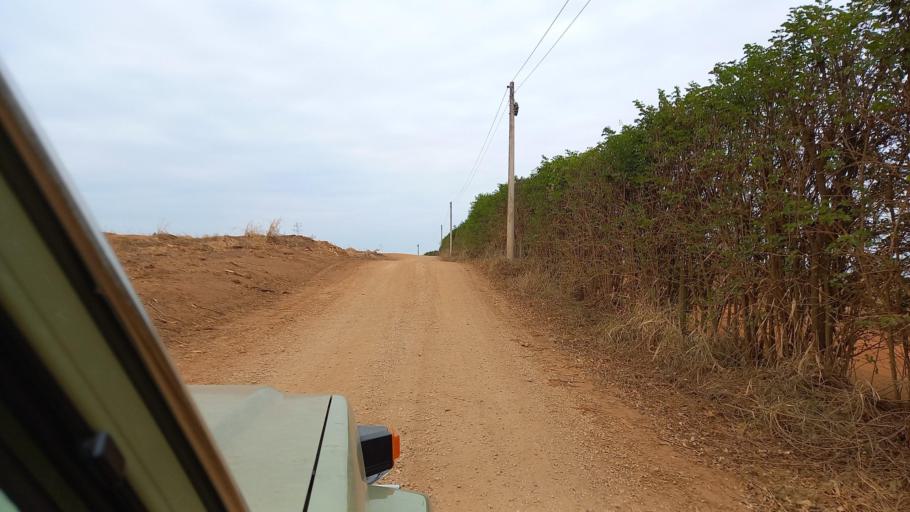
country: BR
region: Sao Paulo
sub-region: Moji-Guacu
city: Mogi-Gaucu
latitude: -22.2784
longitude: -46.8451
